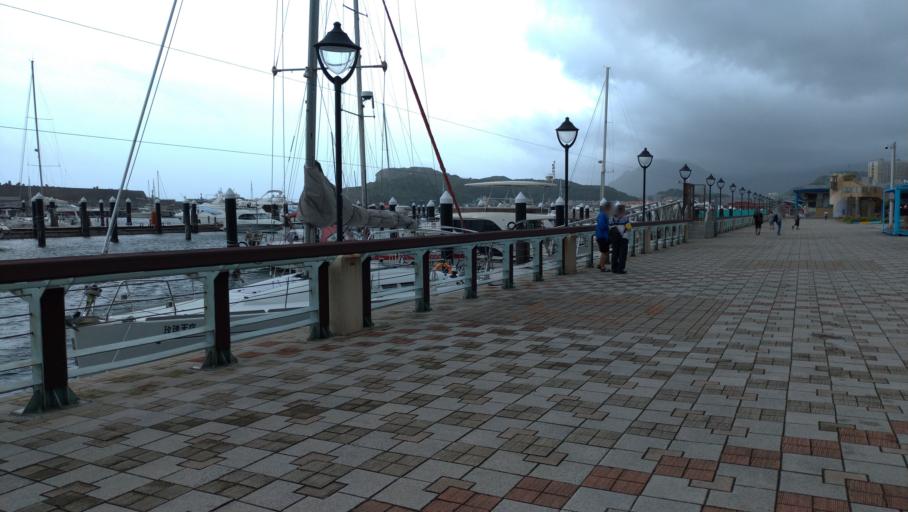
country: TW
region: Taiwan
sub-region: Keelung
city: Keelung
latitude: 25.1469
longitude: 121.7845
